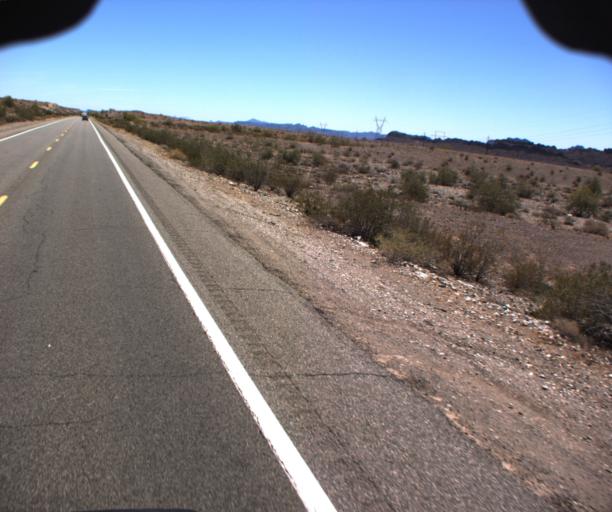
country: US
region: Arizona
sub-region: Mohave County
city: Lake Havasu City
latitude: 34.4448
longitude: -114.2362
